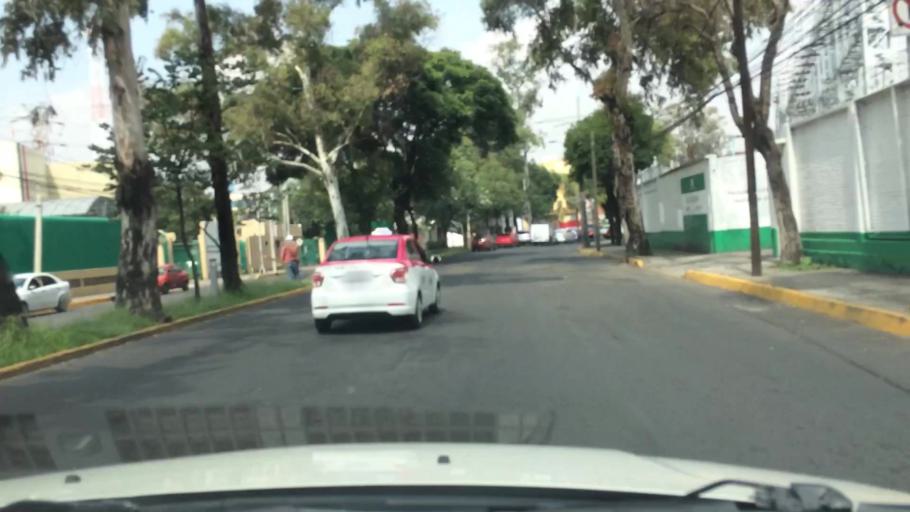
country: MX
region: Mexico City
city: Coyoacan
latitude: 19.3363
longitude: -99.1491
